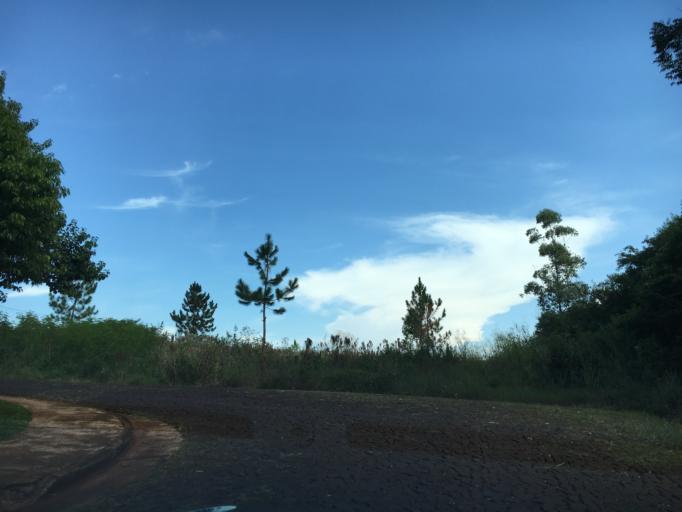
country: AR
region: Misiones
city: Puerto Rico
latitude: -26.8161
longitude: -55.0359
